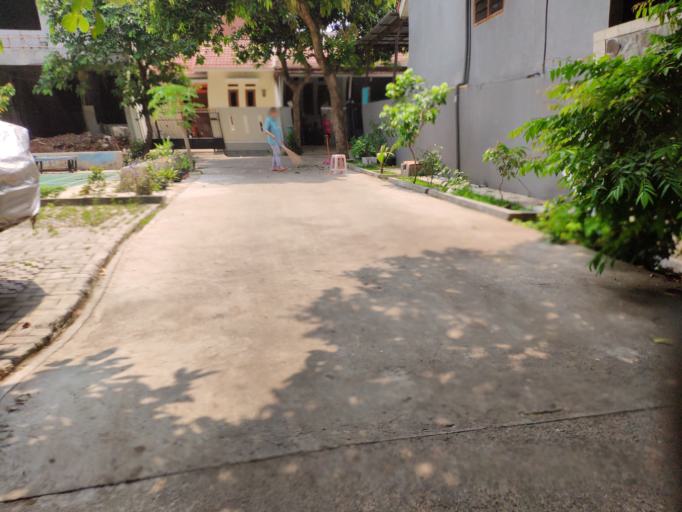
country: ID
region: West Java
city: Sawangan
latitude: -6.3707
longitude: 106.7929
